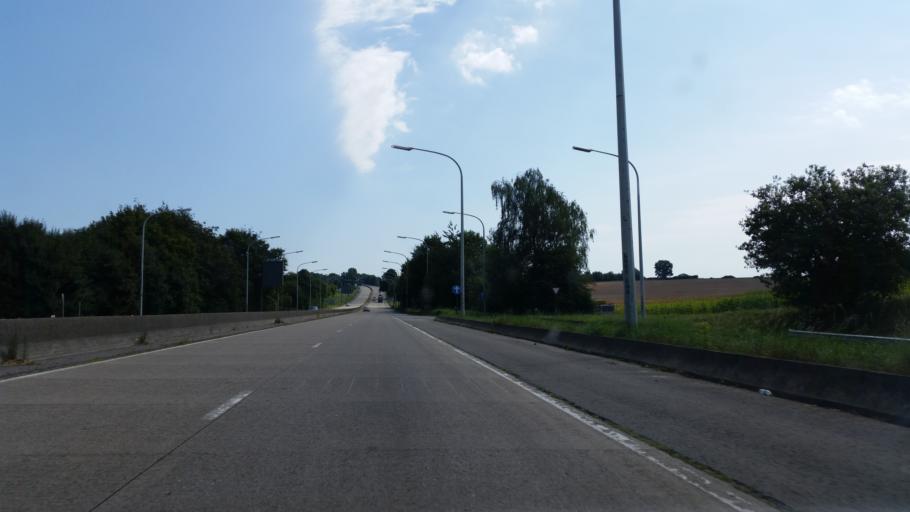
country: BE
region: Wallonia
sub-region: Province de Namur
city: Hamois
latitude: 50.3176
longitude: 5.1309
